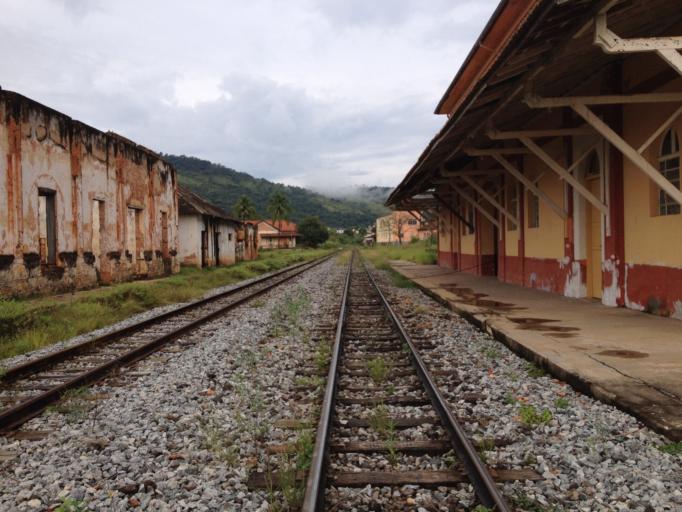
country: BR
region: Minas Gerais
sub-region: Lavras
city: Lavras
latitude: -21.1909
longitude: -45.0591
